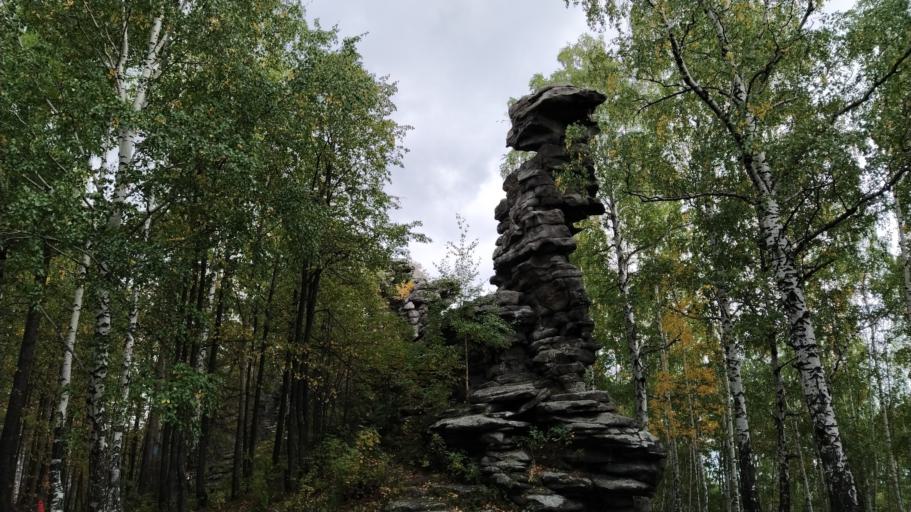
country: RU
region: Sverdlovsk
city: Verkh-Neyvinskiy
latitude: 57.2407
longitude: 60.2290
